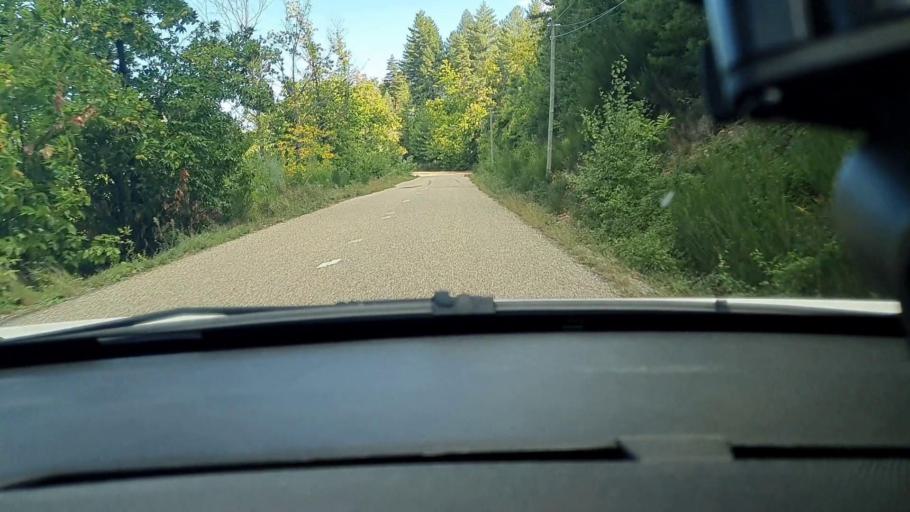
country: FR
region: Rhone-Alpes
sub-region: Departement de l'Ardeche
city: Les Vans
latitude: 44.3936
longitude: 3.9922
